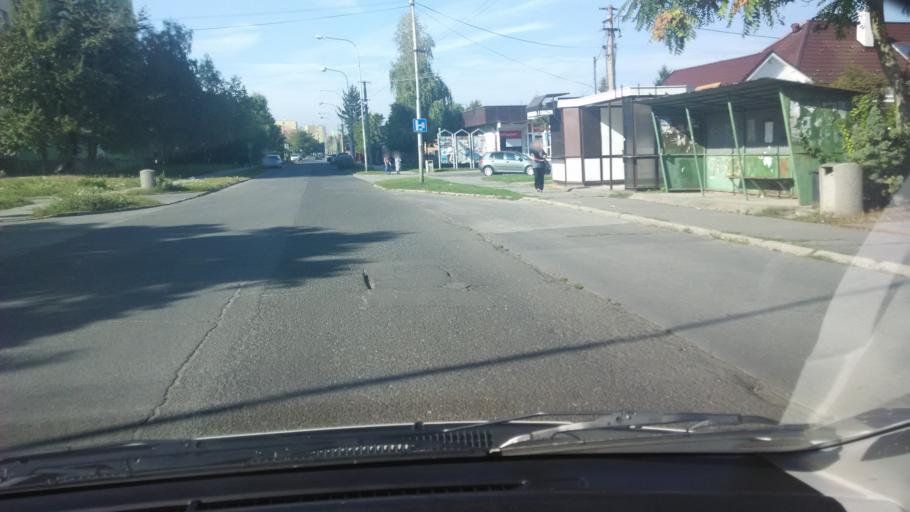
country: SK
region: Nitriansky
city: Levice
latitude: 48.2056
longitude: 18.6128
